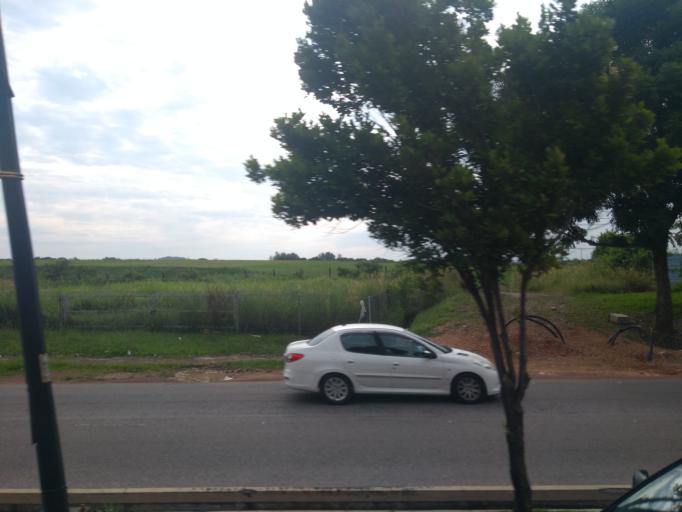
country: MY
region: Melaka
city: Kampung Ayer Keroh
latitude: 2.2738
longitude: 102.2596
